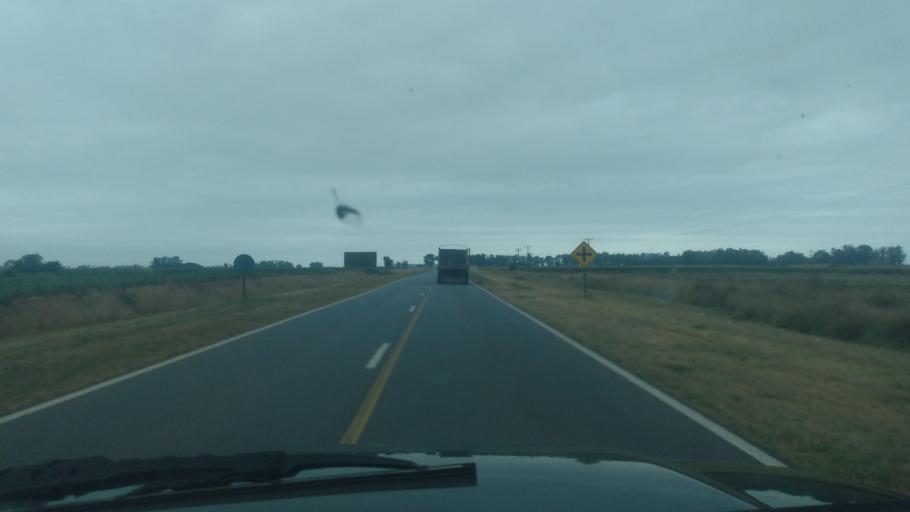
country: AR
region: Buenos Aires
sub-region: Partido de Nueve de Julio
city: Nueve de Julio
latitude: -35.4131
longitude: -60.7793
